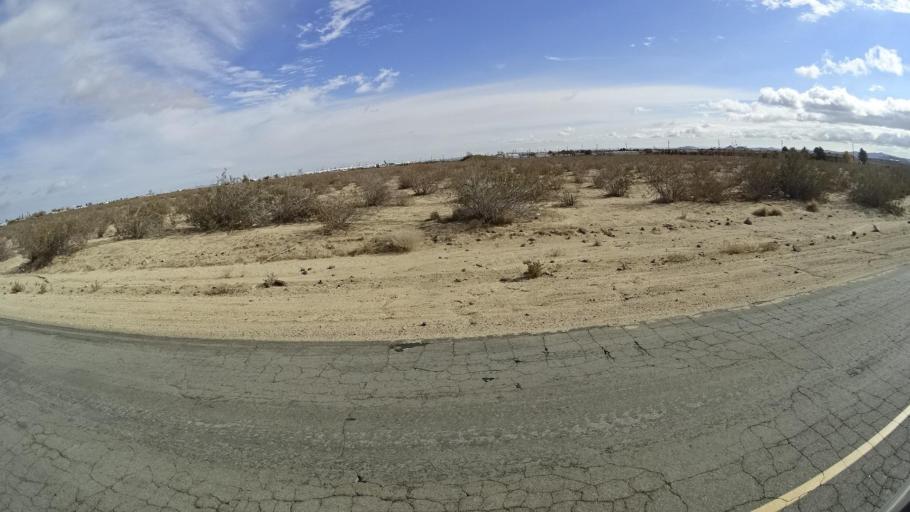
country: US
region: California
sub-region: Kern County
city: Mojave
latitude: 35.0589
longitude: -118.1857
